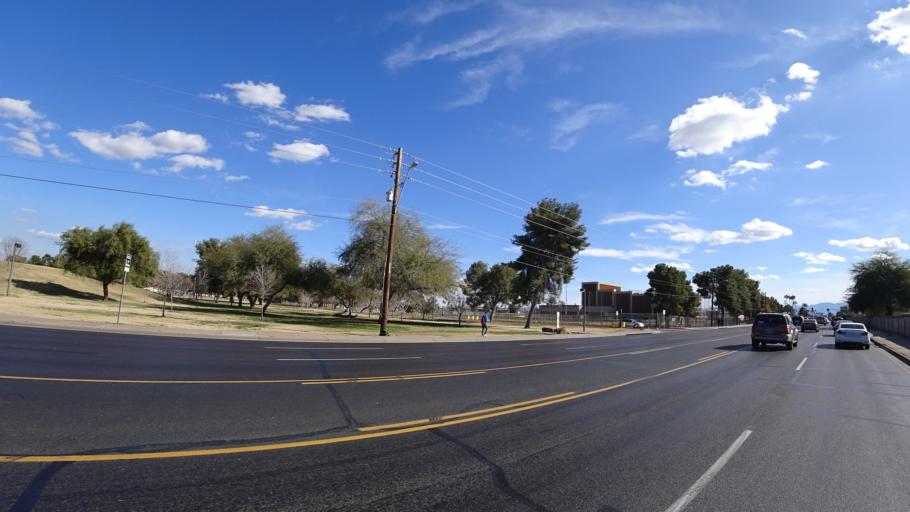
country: US
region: Arizona
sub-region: Maricopa County
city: Tolleson
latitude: 33.4866
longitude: -112.2206
